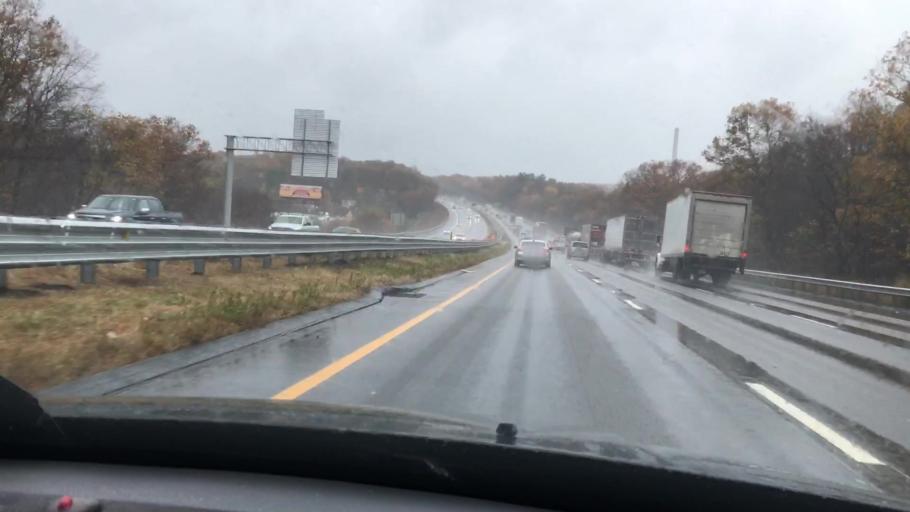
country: US
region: Massachusetts
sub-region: Worcester County
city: Millbury
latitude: 42.2217
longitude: -71.7527
